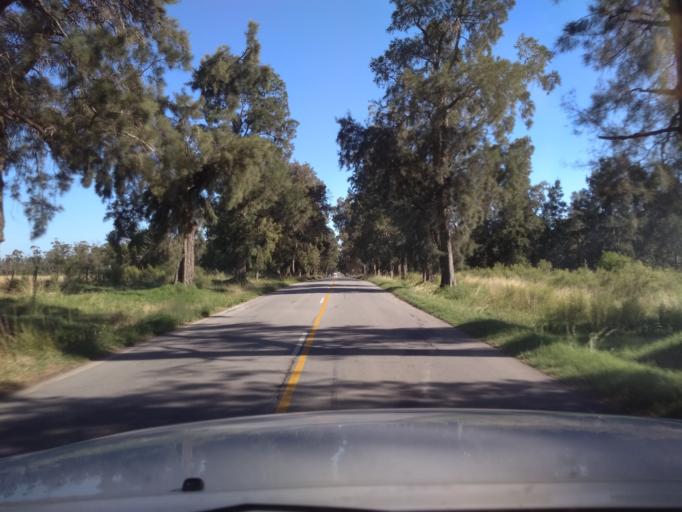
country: UY
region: Canelones
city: San Bautista
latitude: -34.3830
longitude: -55.9595
